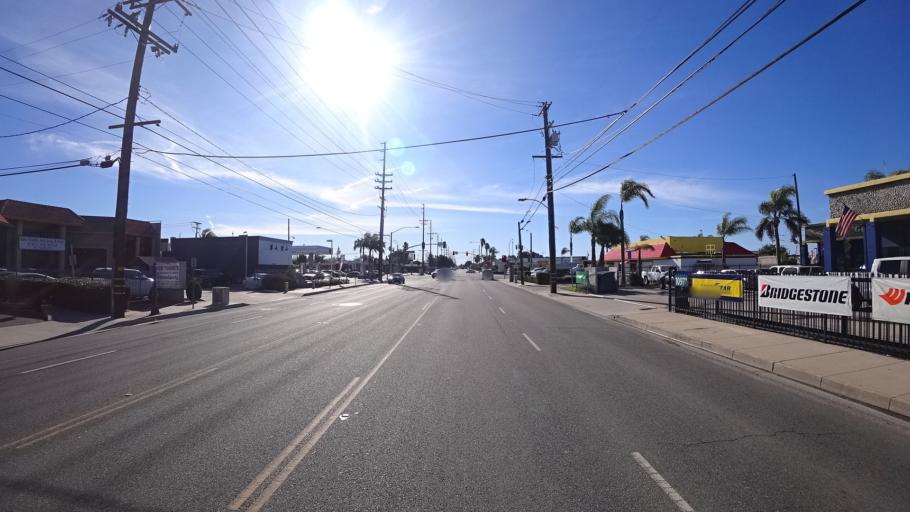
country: US
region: California
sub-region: Orange County
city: Stanton
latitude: 33.8038
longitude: -117.9845
